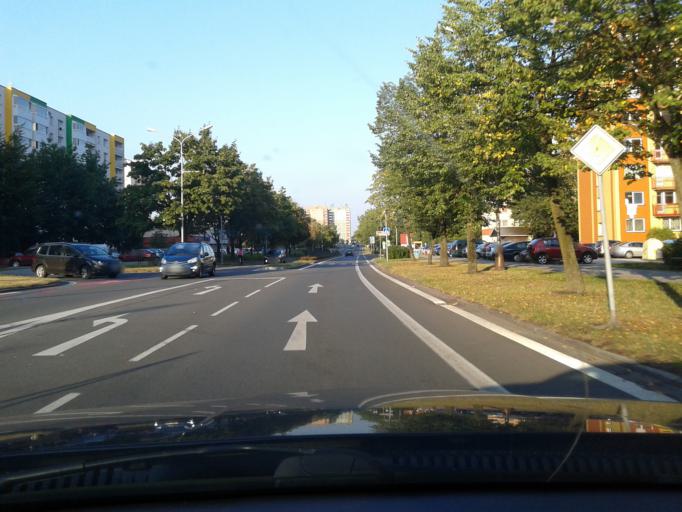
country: CZ
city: Dolni Lutyne
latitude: 49.8748
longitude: 18.4289
